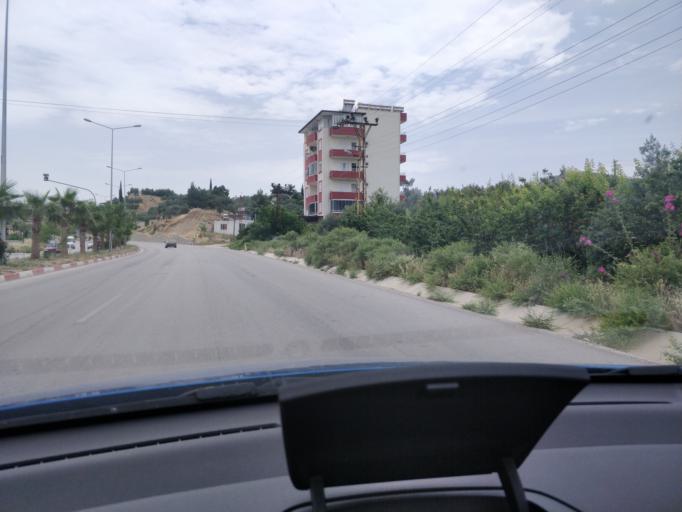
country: TR
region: Mersin
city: Mut
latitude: 36.6583
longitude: 33.4218
